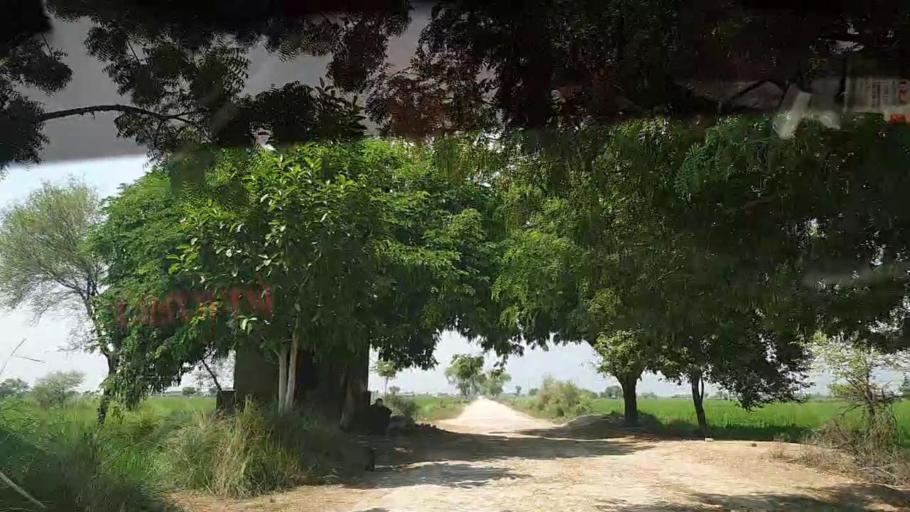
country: PK
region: Sindh
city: Thul
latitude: 28.1730
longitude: 68.7470
